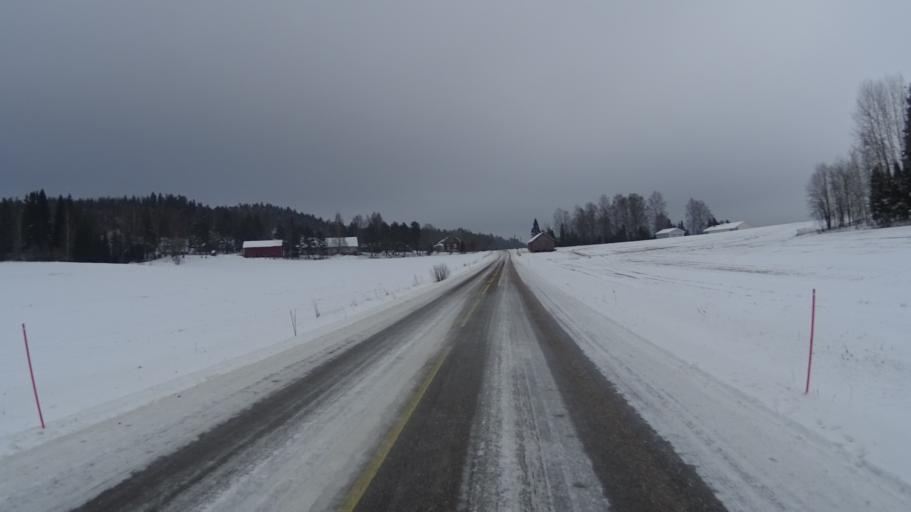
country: FI
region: Uusimaa
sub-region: Helsinki
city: Saukkola
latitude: 60.4064
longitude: 24.1017
